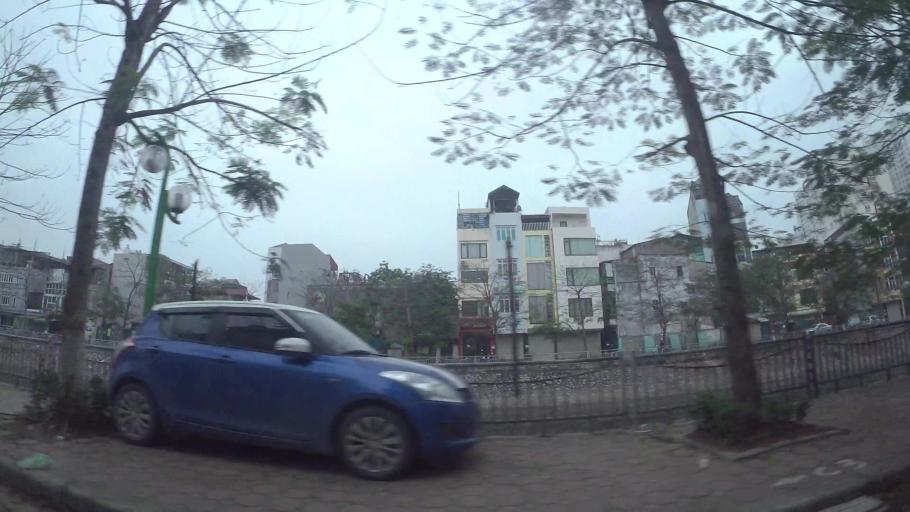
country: VN
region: Ha Noi
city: Hai BaTrung
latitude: 20.9863
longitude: 105.8448
